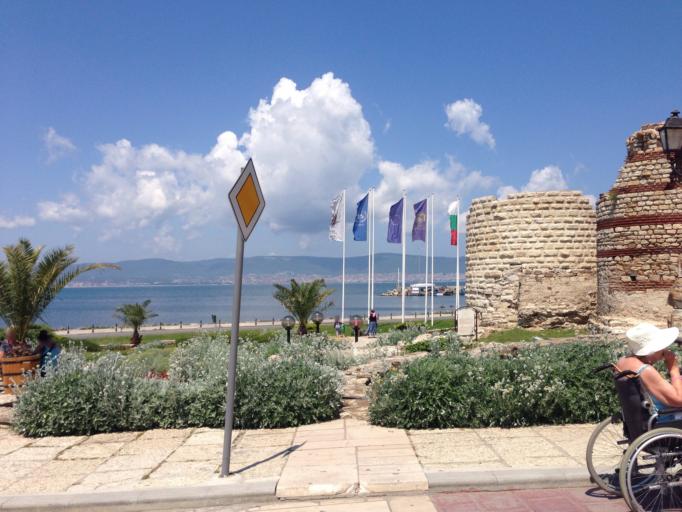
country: BG
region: Burgas
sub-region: Obshtina Nesebur
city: Nesebar
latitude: 42.6588
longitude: 27.7304
